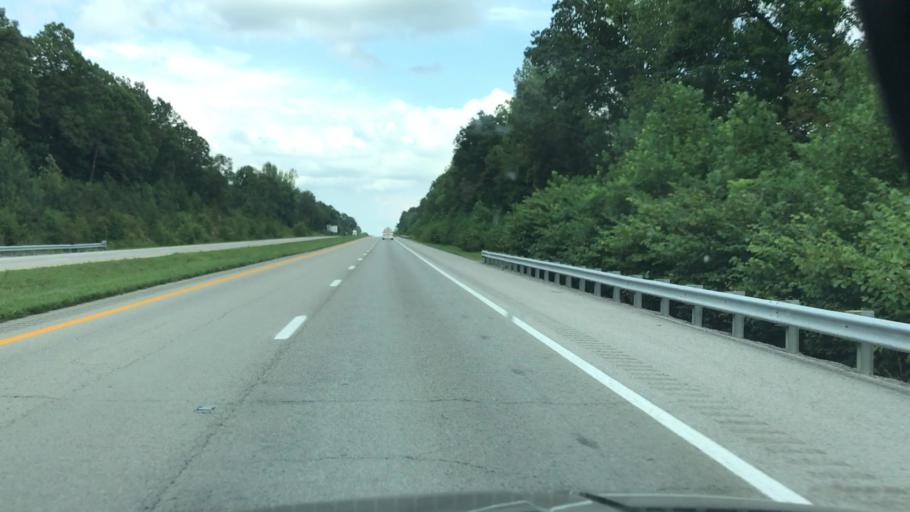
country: US
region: Kentucky
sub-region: Hopkins County
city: Dawson Springs
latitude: 37.1974
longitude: -87.6514
